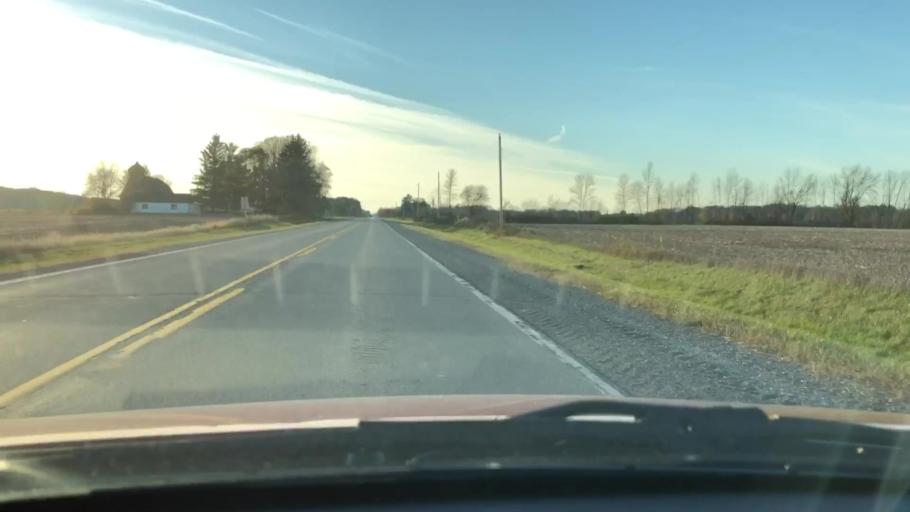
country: US
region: Wisconsin
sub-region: Brown County
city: Oneida
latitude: 44.4442
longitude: -88.1927
